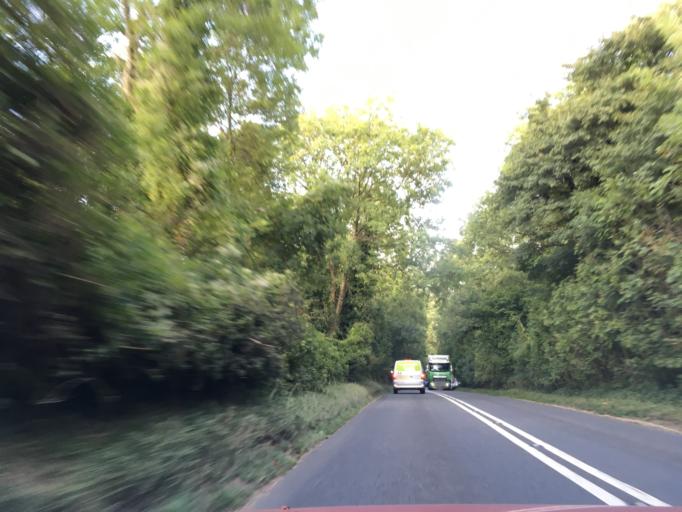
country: GB
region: England
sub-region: Gloucestershire
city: Bourton on the Water
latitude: 51.8794
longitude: -1.7792
